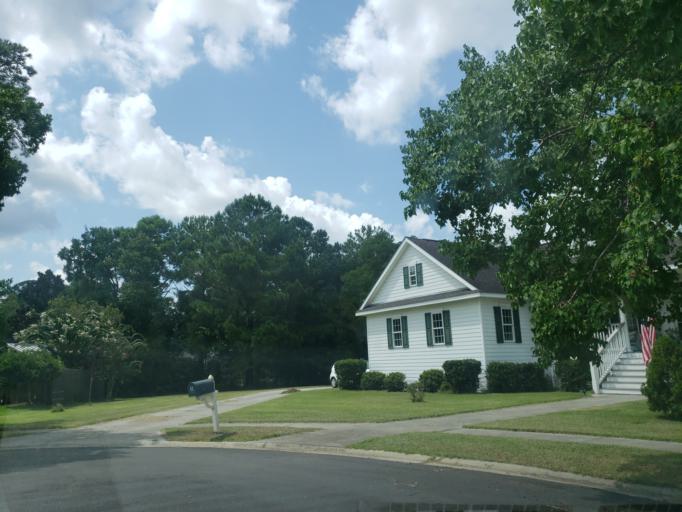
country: US
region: Georgia
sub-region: Chatham County
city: Isle of Hope
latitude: 31.9880
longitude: -81.0478
